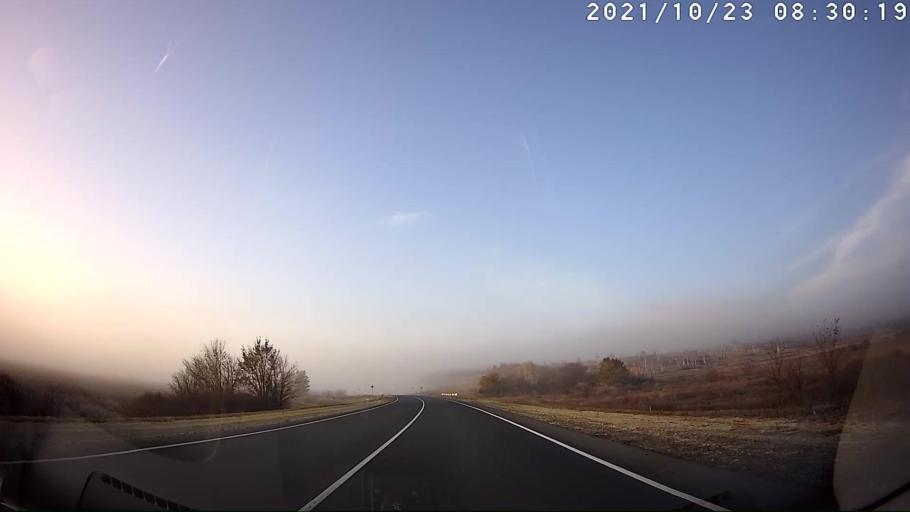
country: RU
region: Saratov
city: Sennoy
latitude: 52.1019
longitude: 46.8156
